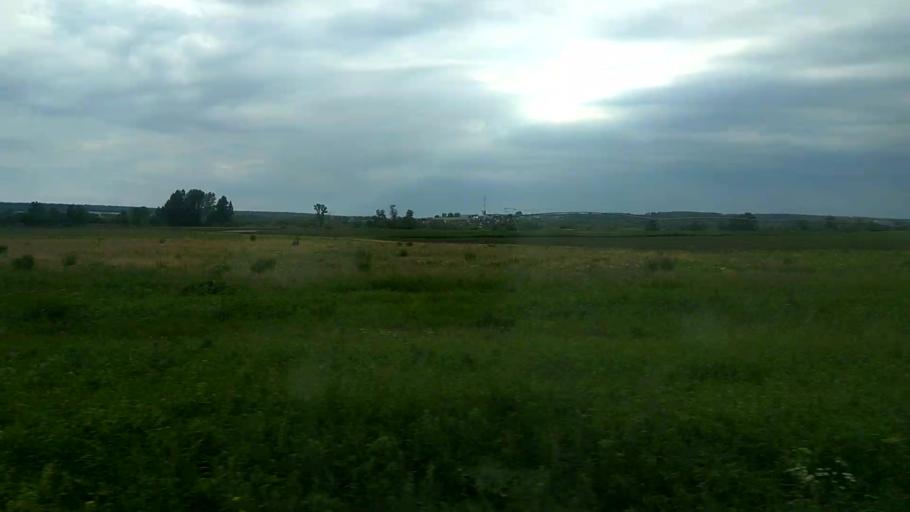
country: RU
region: Moskovskaya
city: Ozery
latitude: 54.8429
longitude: 38.5715
